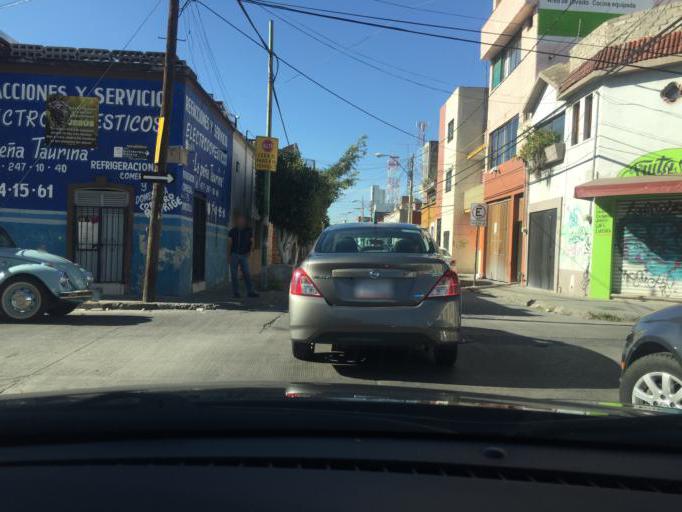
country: MX
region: Guanajuato
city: Leon
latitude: 21.1269
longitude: -101.6785
